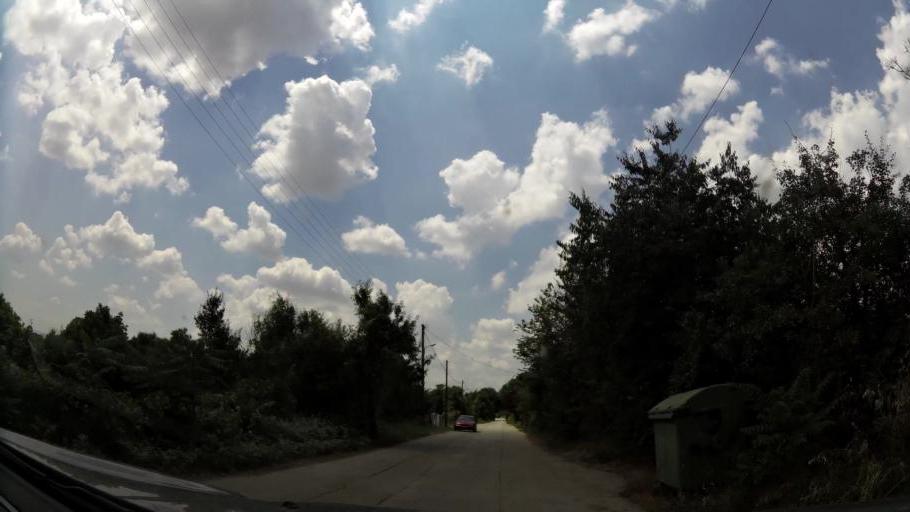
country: GR
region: West Macedonia
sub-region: Nomos Kozanis
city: Kozani
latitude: 40.2866
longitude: 21.7803
